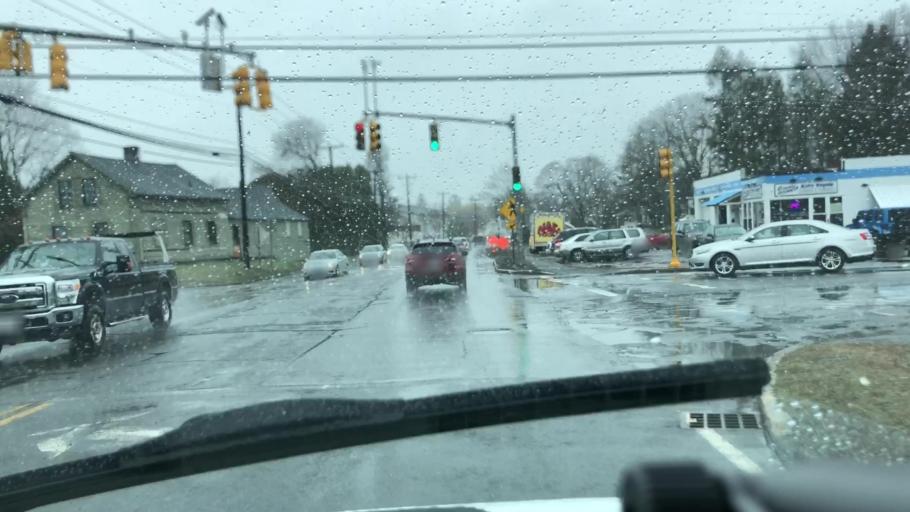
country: US
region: Massachusetts
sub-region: Hampshire County
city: Hadley
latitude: 42.3430
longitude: -72.5817
